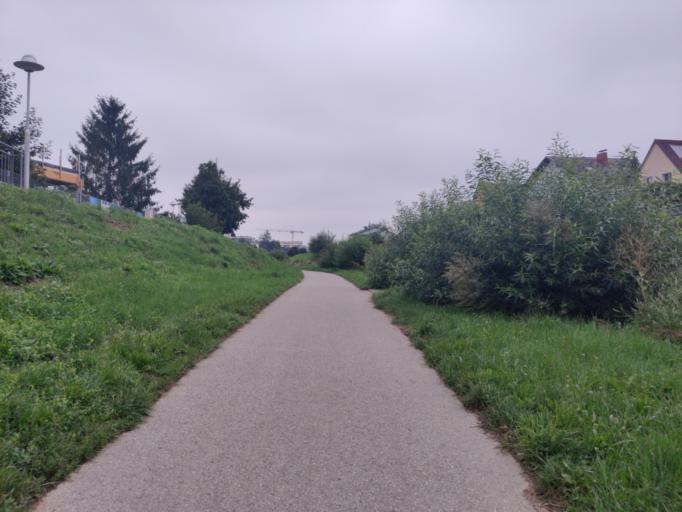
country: AT
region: Lower Austria
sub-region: Krems an der Donau Stadt
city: Krems an der Donau
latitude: 48.4102
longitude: 15.6122
